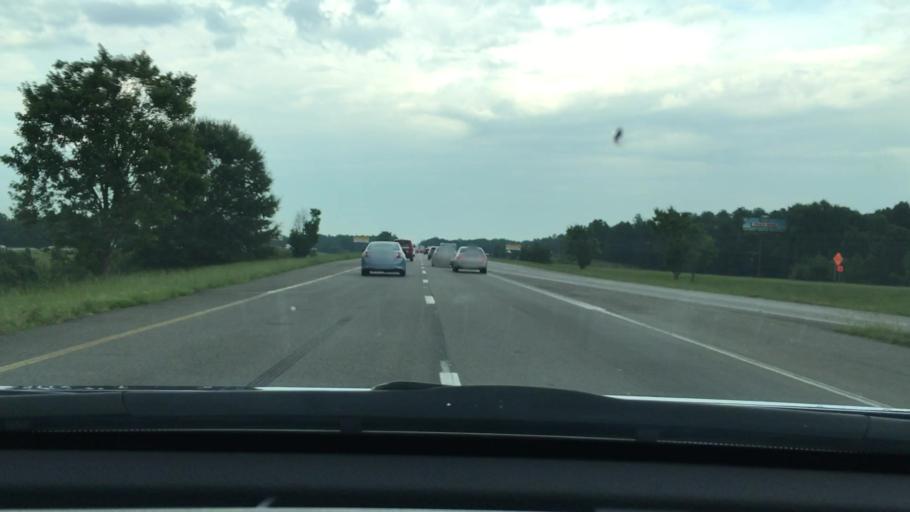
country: US
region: South Carolina
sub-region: Lexington County
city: Cayce
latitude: 33.9278
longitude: -81.0654
